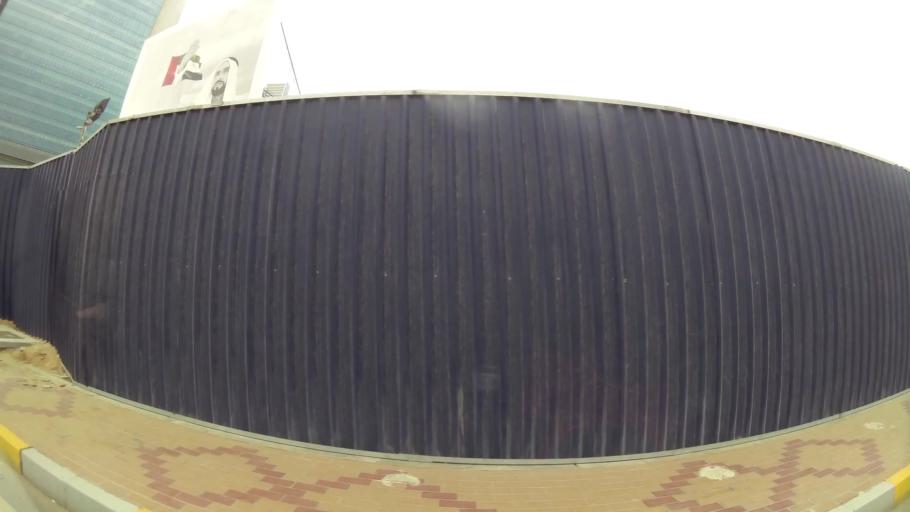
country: AE
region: Abu Dhabi
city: Abu Dhabi
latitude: 24.4632
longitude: 54.3238
